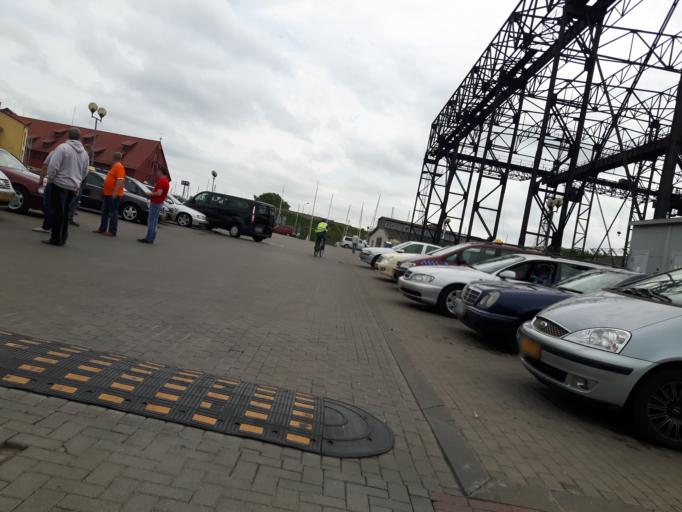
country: LT
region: Klaipedos apskritis
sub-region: Klaipeda
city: Klaipeda
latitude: 55.7055
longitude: 21.1242
